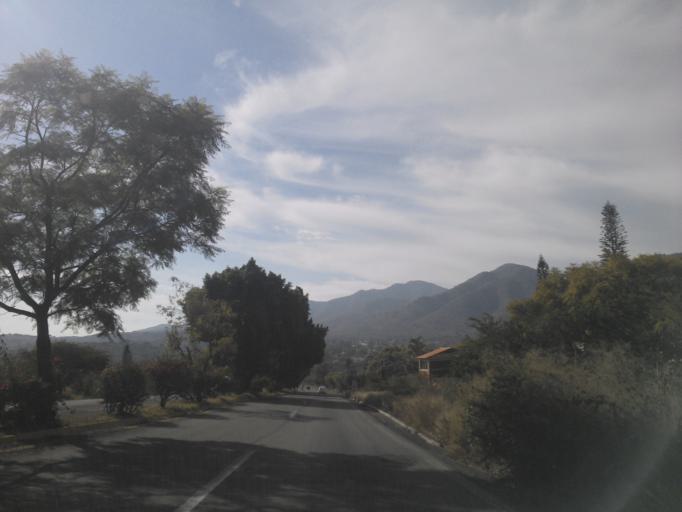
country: MX
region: Jalisco
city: Ixtlahuacan de los Membrillos
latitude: 20.3272
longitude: -103.1885
